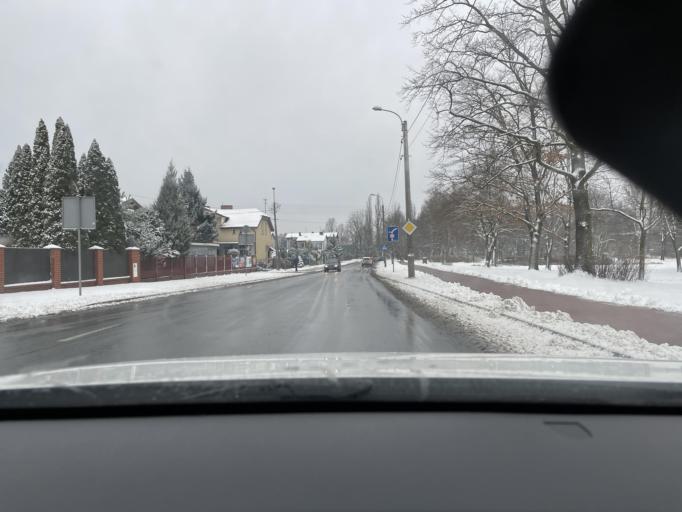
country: PL
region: Masovian Voivodeship
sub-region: Powiat zyrardowski
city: Zyrardow
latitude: 52.0471
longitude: 20.4400
